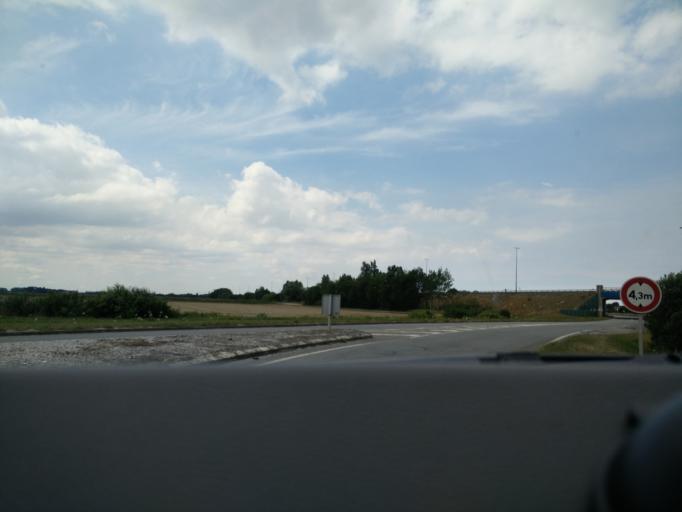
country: FR
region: Nord-Pas-de-Calais
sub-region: Departement du Nord
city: Ghyvelde
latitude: 51.0454
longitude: 2.5328
